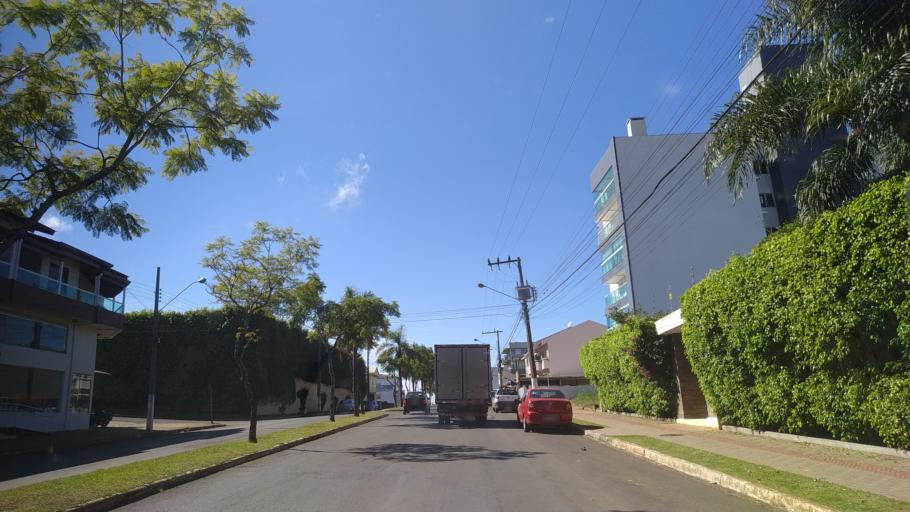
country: BR
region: Santa Catarina
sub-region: Chapeco
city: Chapeco
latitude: -27.1055
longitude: -52.6027
